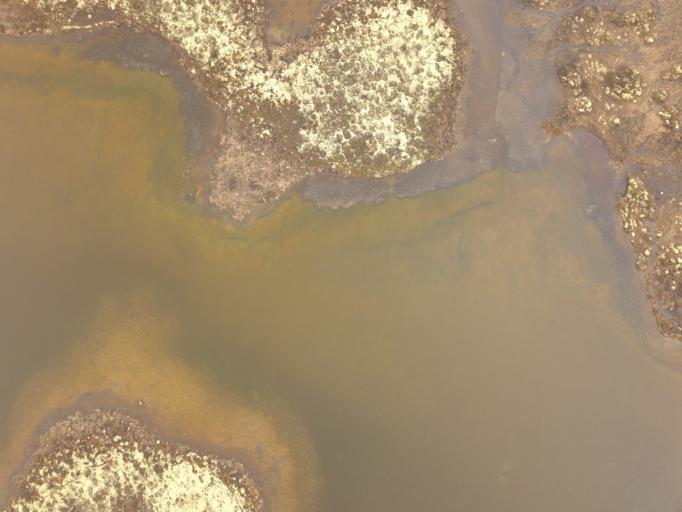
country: NO
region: Hedmark
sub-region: Folldal
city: Folldal
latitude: 62.2277
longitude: 9.6453
